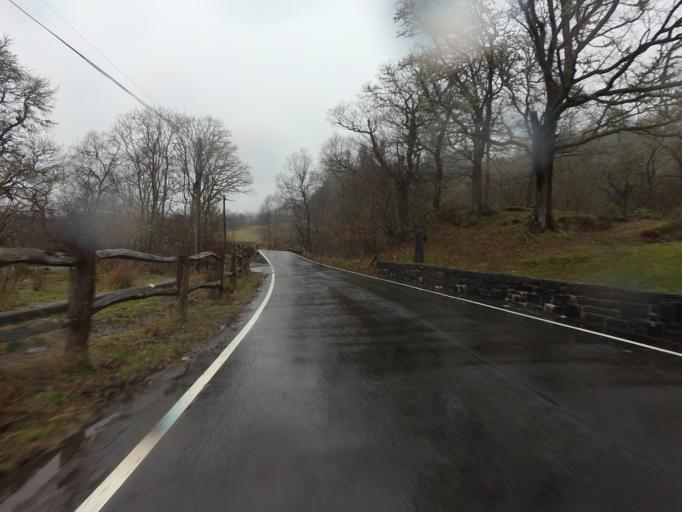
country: GB
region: Scotland
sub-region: West Dunbartonshire
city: Balloch
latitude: 56.1945
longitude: -4.5157
